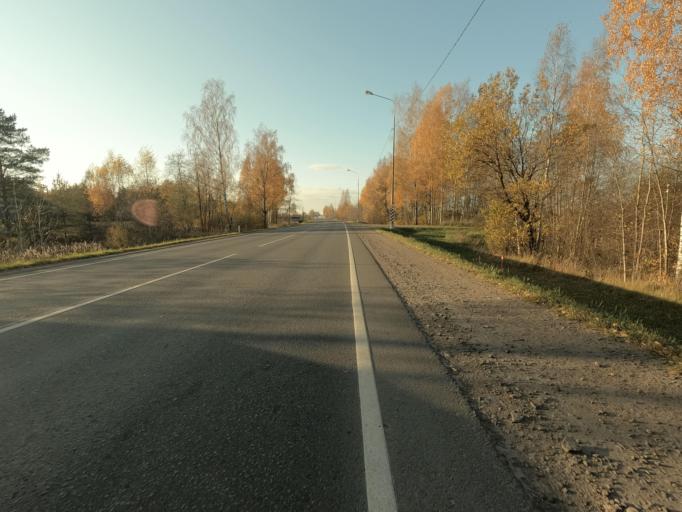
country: RU
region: Leningrad
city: Kirovsk
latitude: 59.8586
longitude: 31.0062
